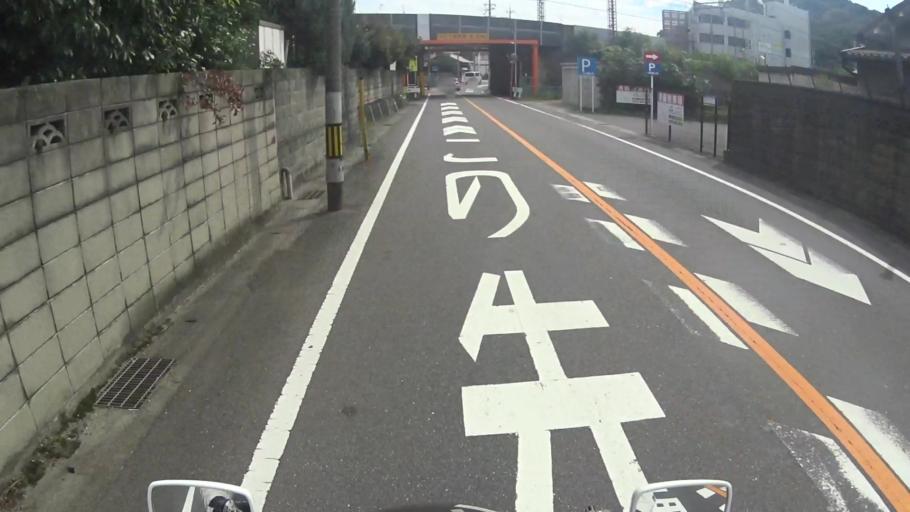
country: JP
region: Kyoto
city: Yawata
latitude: 34.8860
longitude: 135.7031
